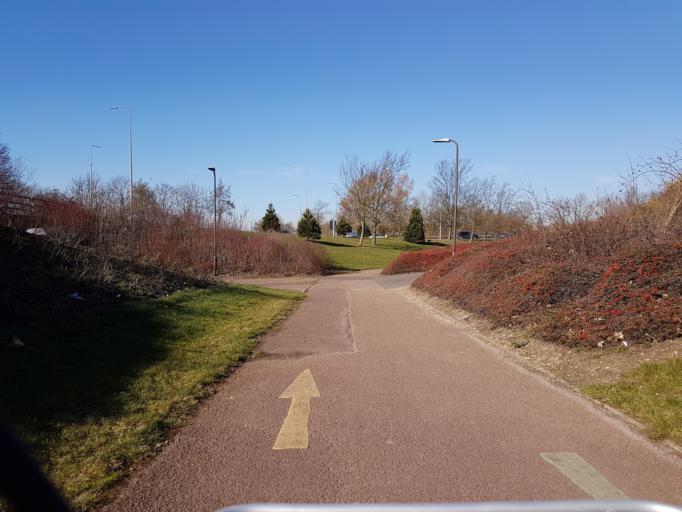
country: GB
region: England
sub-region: Milton Keynes
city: Milton Keynes
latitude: 52.0251
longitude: -0.7569
